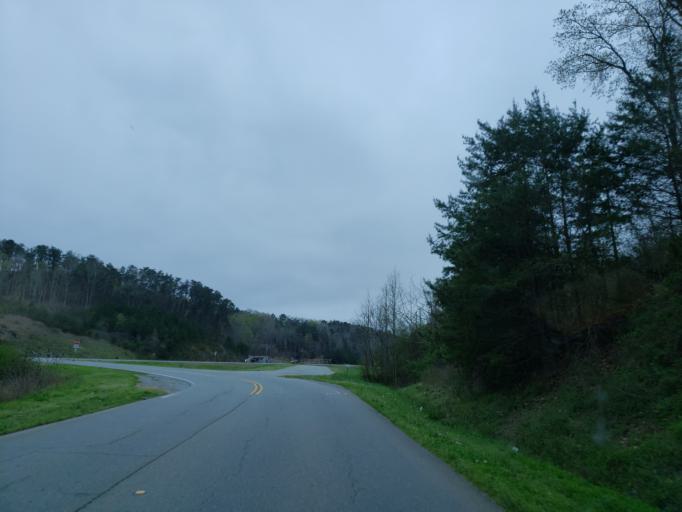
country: US
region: Georgia
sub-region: Polk County
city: Aragon
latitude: 34.0741
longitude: -84.9868
